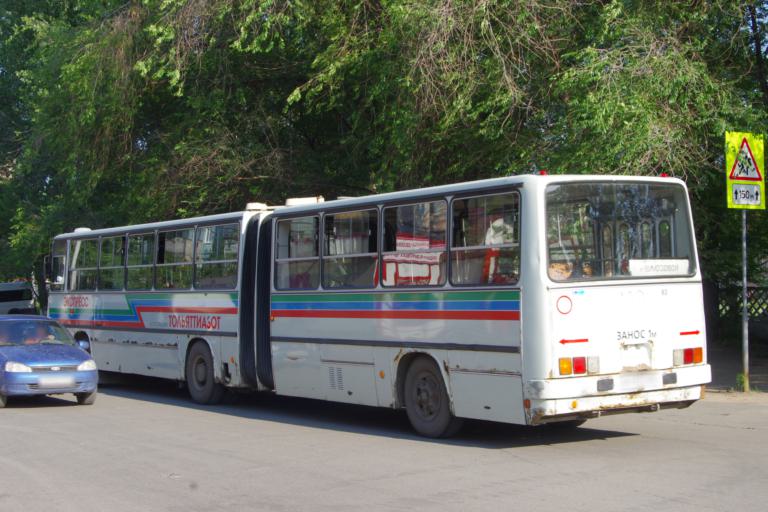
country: RU
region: Samara
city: Zhigulevsk
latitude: 53.4647
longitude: 49.5361
